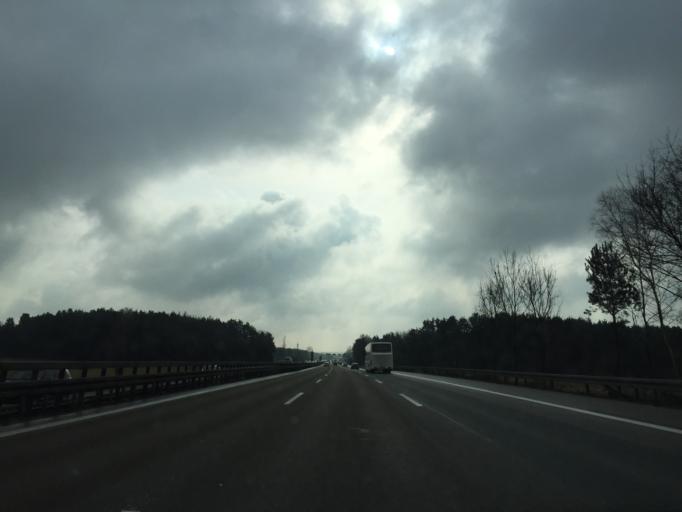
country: DE
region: Bavaria
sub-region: Upper Bavaria
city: Manching
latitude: 48.6926
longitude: 11.4928
